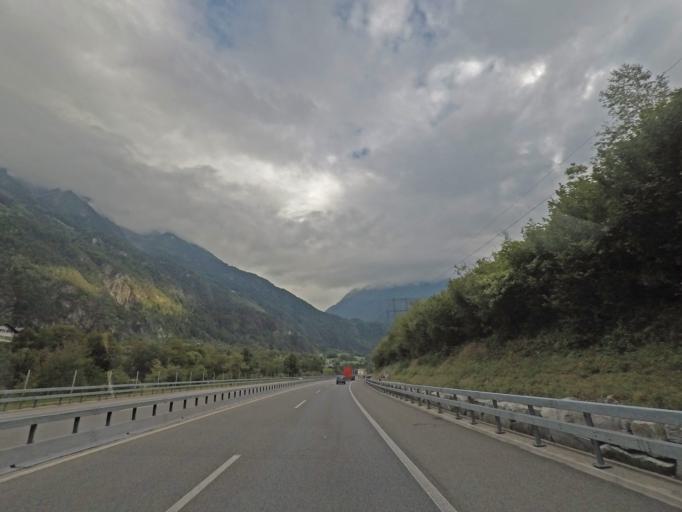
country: CH
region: Uri
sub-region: Uri
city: Silenen
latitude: 46.8009
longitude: 8.6626
